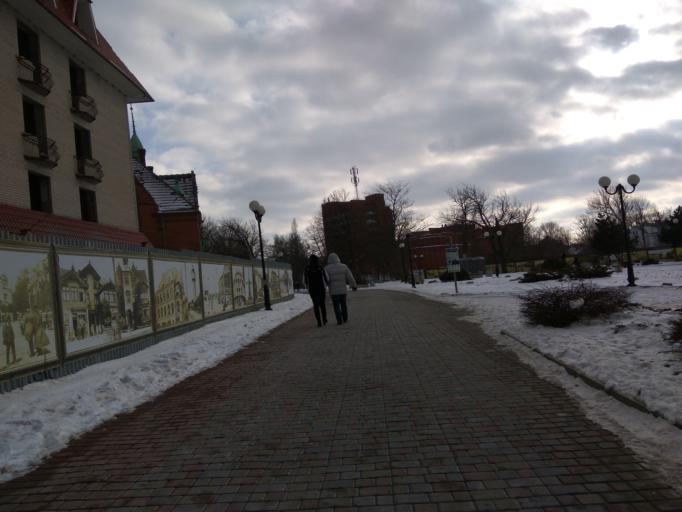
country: RU
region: Kaliningrad
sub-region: Zelenogradskiy Rayon
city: Zelenogradsk
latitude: 54.9621
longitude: 20.4756
